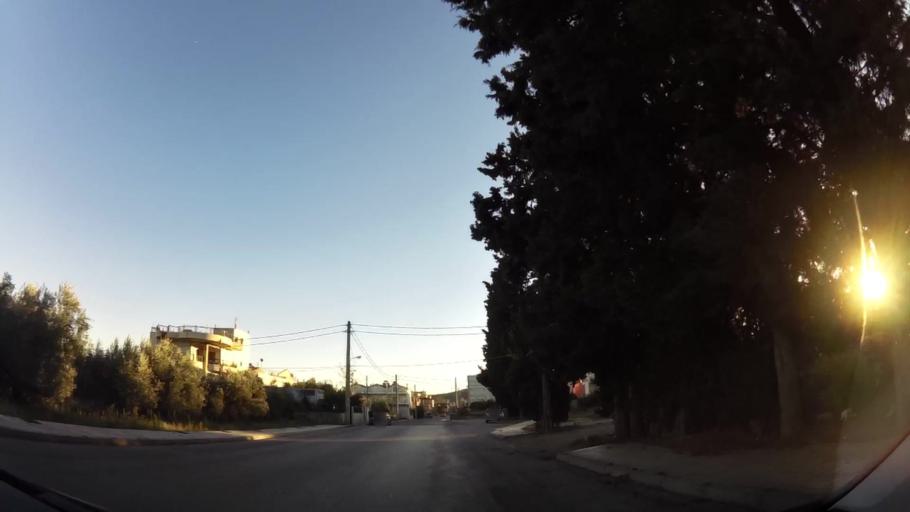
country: GR
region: Attica
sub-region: Nomarchia Dytikis Attikis
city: Ano Liosia
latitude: 38.0842
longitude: 23.7112
